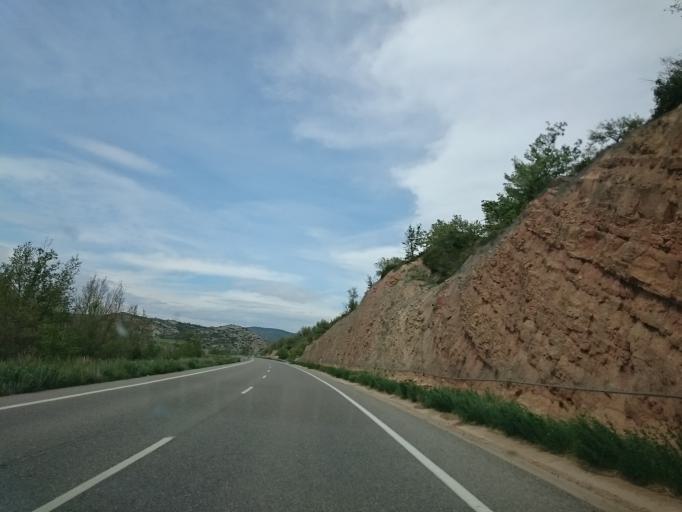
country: ES
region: Catalonia
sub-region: Provincia de Lleida
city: Tora de Riubregos
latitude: 41.8170
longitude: 1.3234
